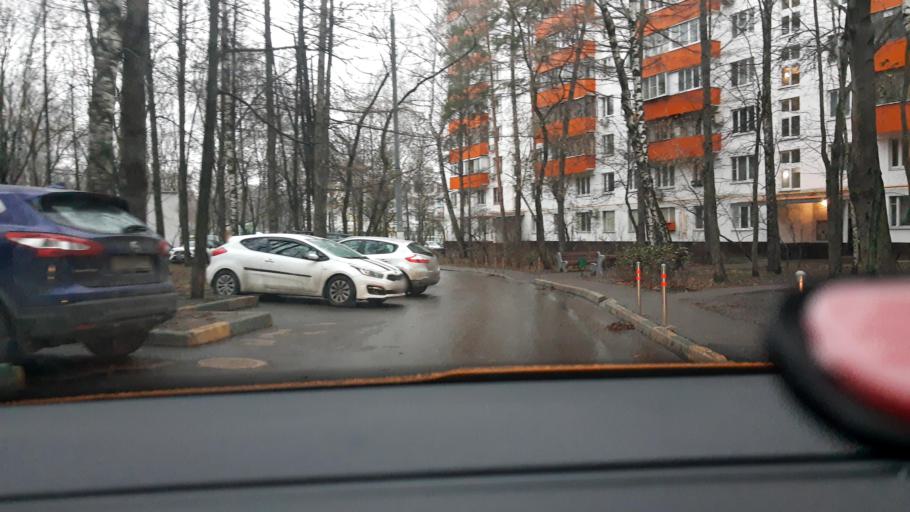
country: RU
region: Moscow
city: Strogino
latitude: 55.8514
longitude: 37.4112
